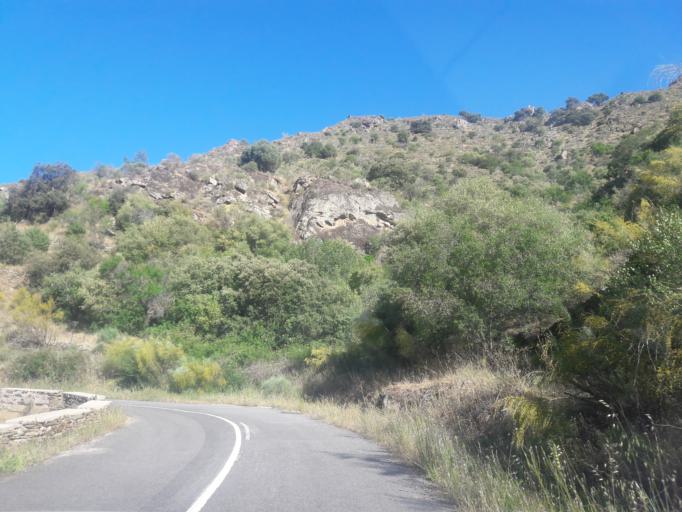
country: ES
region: Castille and Leon
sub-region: Provincia de Salamanca
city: Saucelle
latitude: 41.0303
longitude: -6.7323
